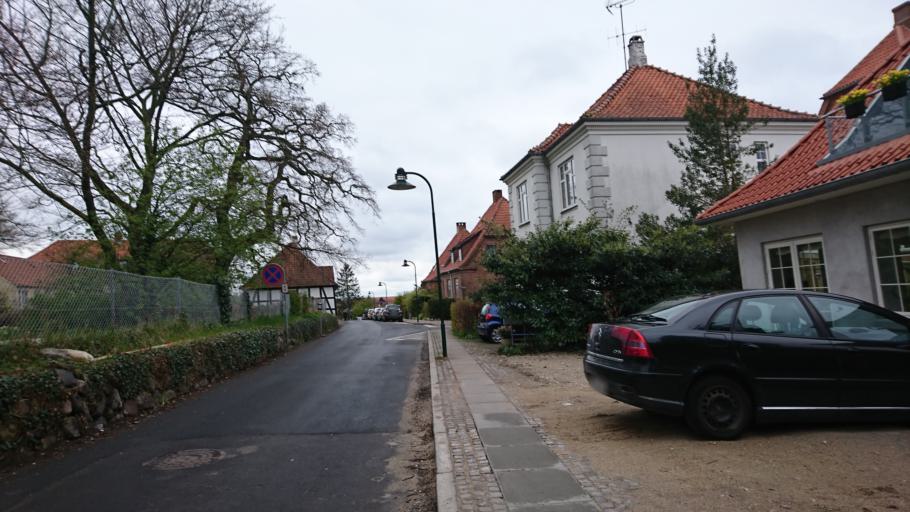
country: DK
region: Zealand
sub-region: Roskilde Kommune
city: Roskilde
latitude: 55.6436
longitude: 12.0823
